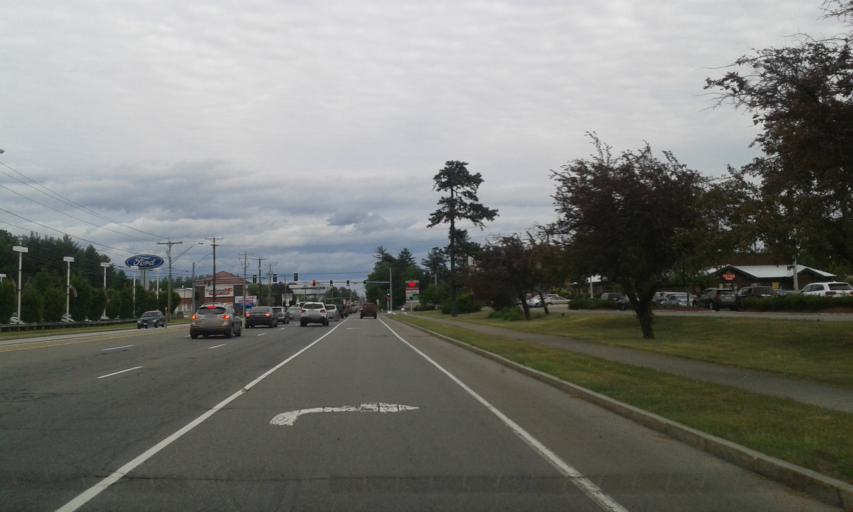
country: US
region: New Hampshire
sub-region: Hillsborough County
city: Litchfield
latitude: 42.7998
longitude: -71.5352
